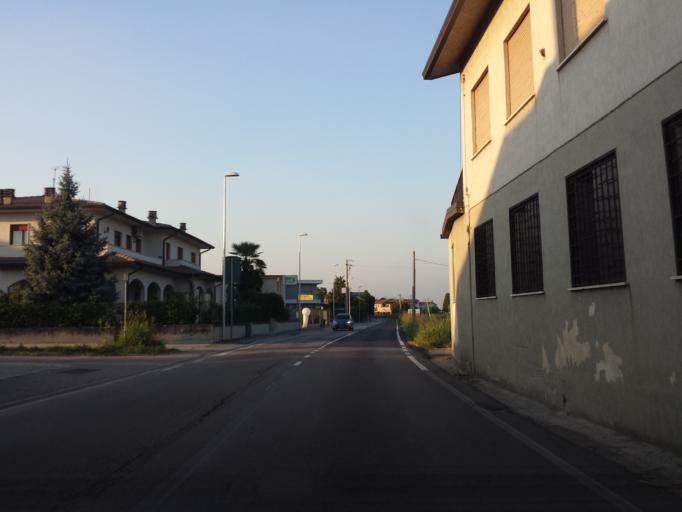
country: IT
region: Veneto
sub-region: Provincia di Vicenza
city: Vicenza
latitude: 45.5711
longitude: 11.5590
